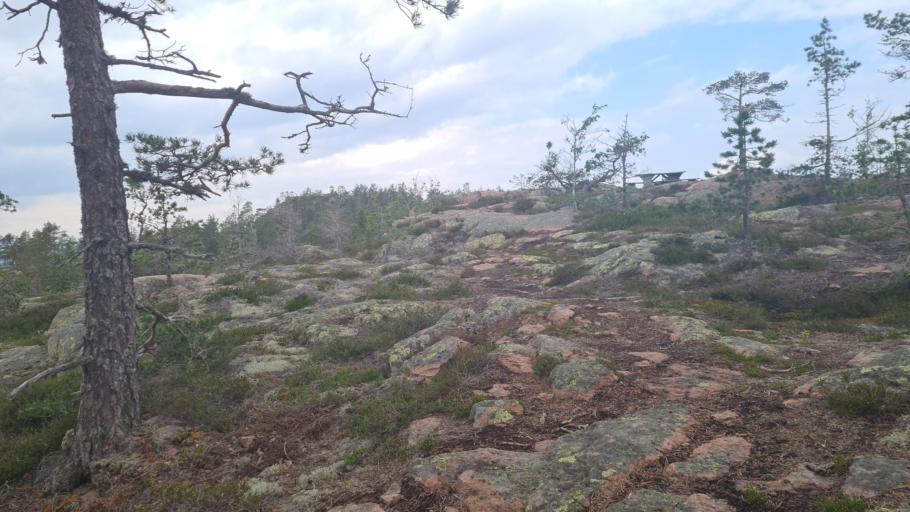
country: SE
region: Vaesternorrland
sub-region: Kramfors Kommun
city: Nordingra
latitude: 62.9837
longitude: 18.3919
